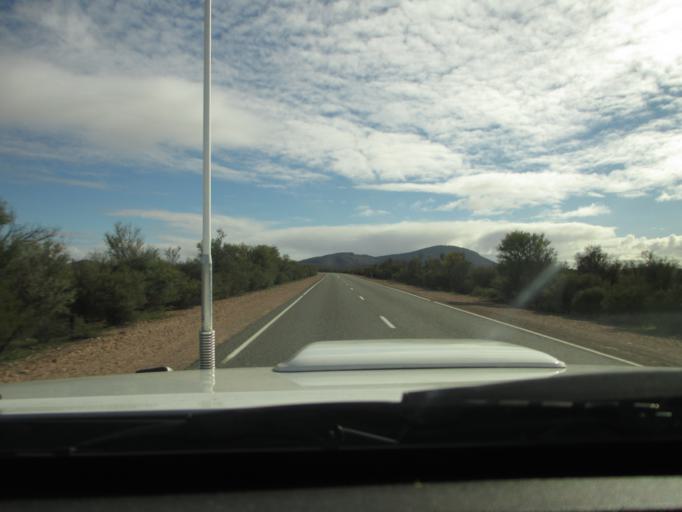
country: AU
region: South Australia
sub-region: Flinders Ranges
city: Quorn
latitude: -31.8265
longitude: 138.3830
